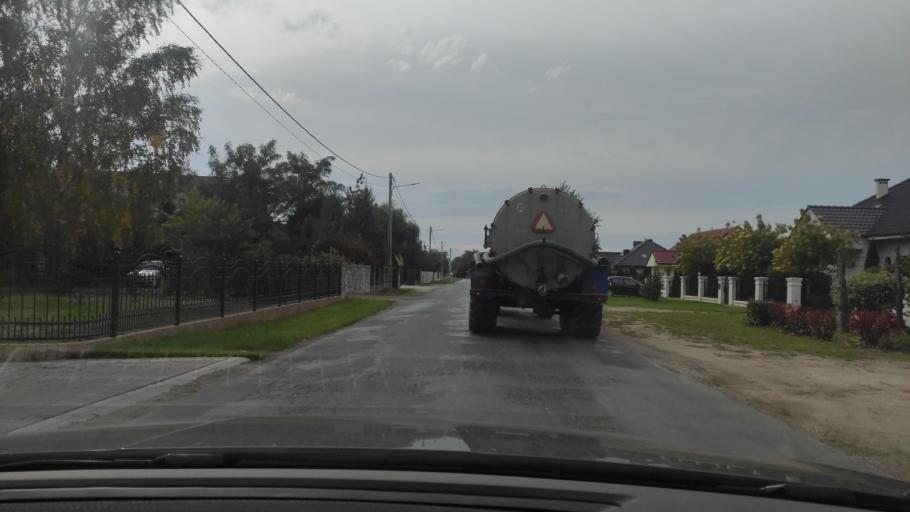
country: PL
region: Greater Poland Voivodeship
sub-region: Powiat poznanski
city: Kleszczewo
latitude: 52.3711
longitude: 17.1516
